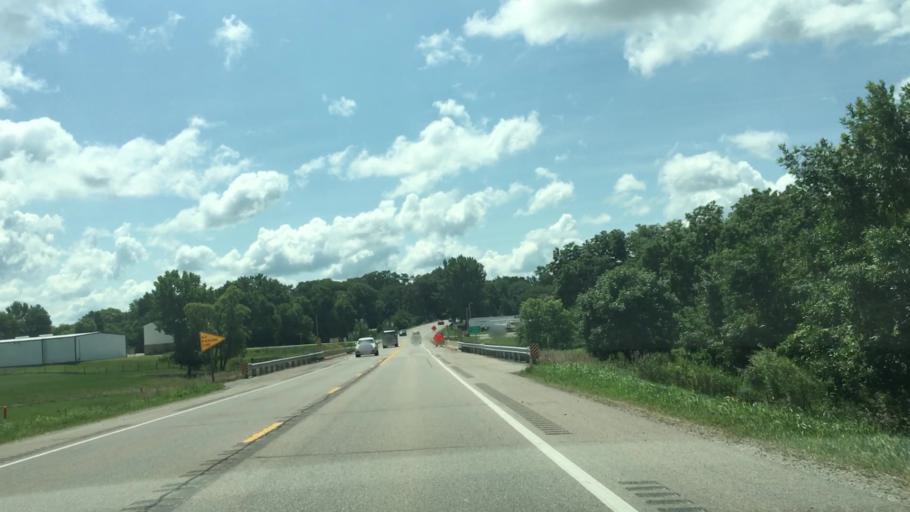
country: US
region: Iowa
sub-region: Johnson County
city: Solon
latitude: 41.8132
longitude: -91.4944
